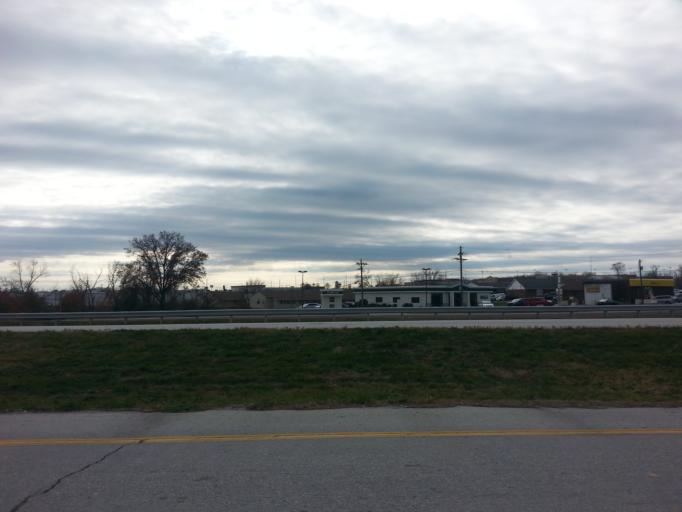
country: US
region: Missouri
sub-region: Marion County
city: Hannibal
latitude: 39.7280
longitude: -91.3937
